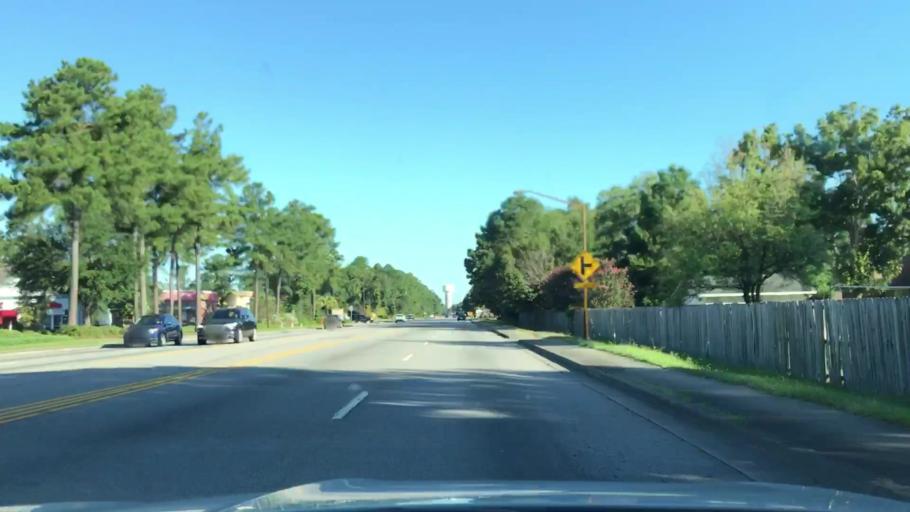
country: US
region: South Carolina
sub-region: Berkeley County
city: Goose Creek
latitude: 33.0239
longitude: -80.0548
